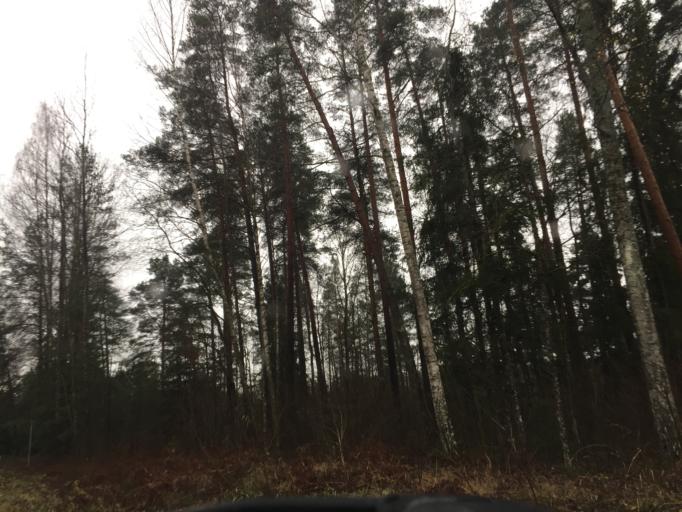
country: LV
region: Salas
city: Sala
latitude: 56.4985
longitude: 25.7778
